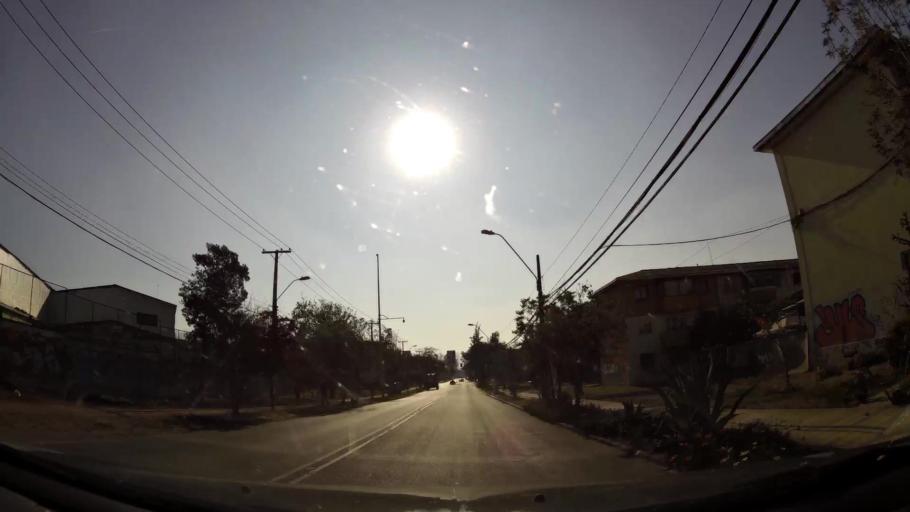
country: CL
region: Santiago Metropolitan
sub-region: Provincia de Santiago
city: Santiago
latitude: -33.4207
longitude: -70.6683
